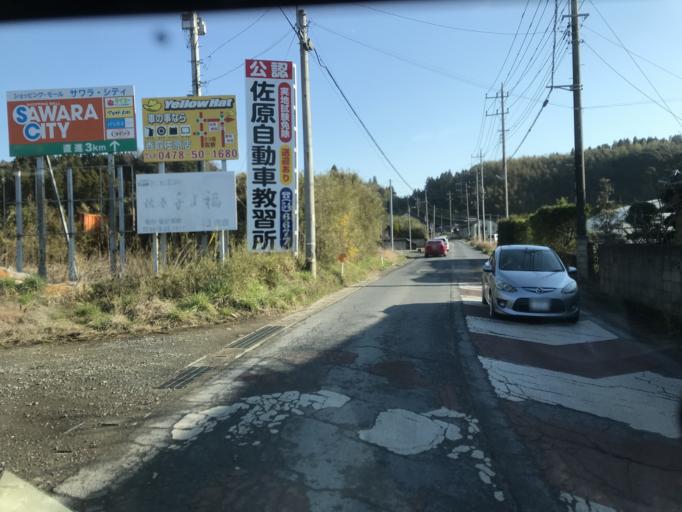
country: JP
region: Chiba
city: Sawara
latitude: 35.8761
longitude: 140.4948
